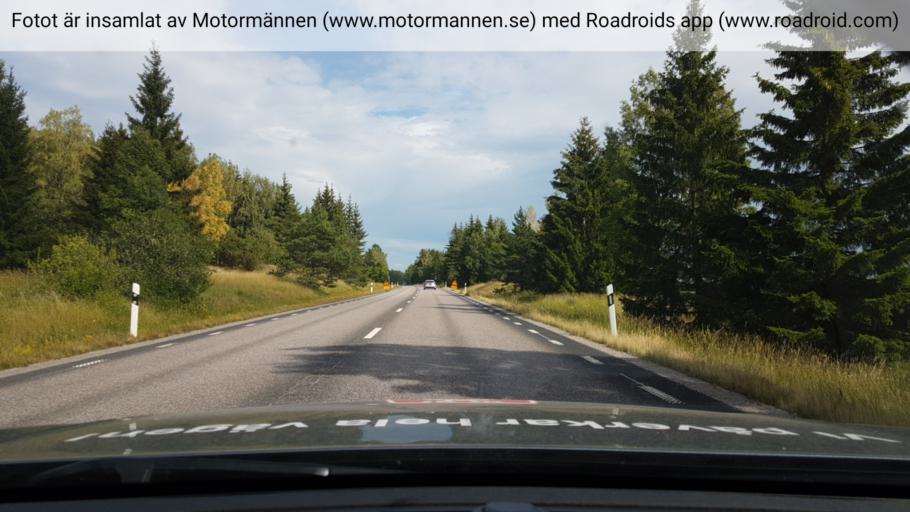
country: SE
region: Uppsala
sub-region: Enkopings Kommun
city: Orsundsbro
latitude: 59.8638
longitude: 17.3471
